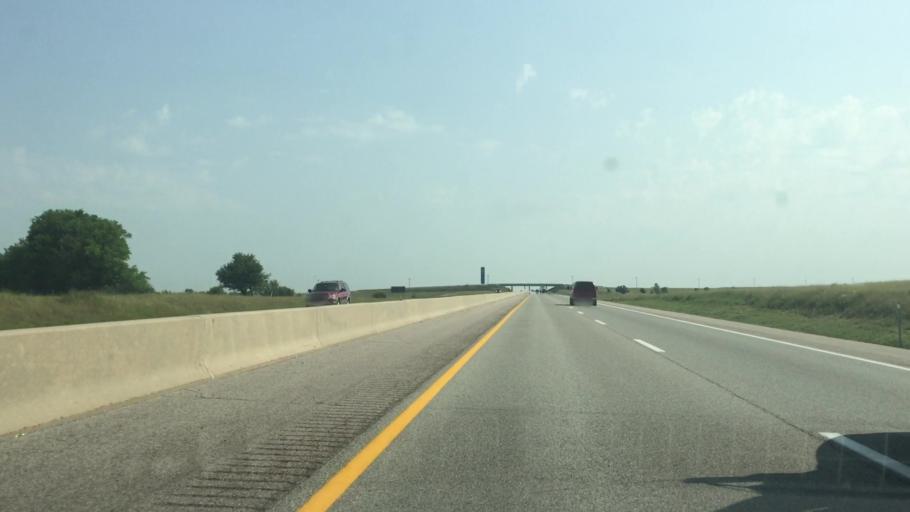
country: US
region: Kansas
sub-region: Butler County
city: El Dorado
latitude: 37.9796
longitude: -96.7126
